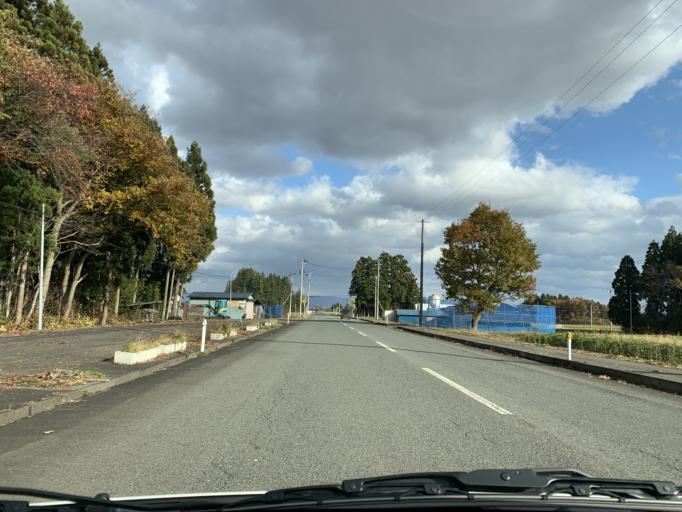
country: JP
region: Iwate
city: Mizusawa
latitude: 39.1119
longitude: 141.0219
